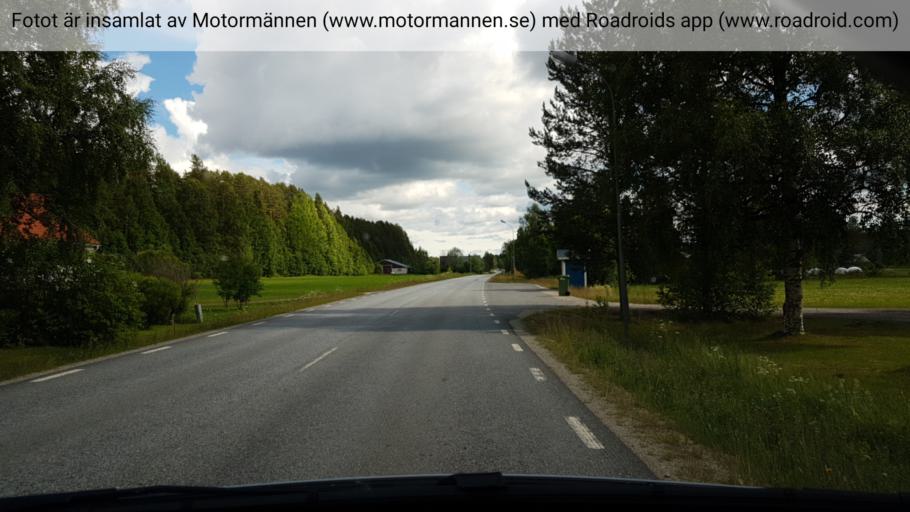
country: SE
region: Vaesterbotten
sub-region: Bjurholms Kommun
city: Bjurholm
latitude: 64.2244
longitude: 19.3663
